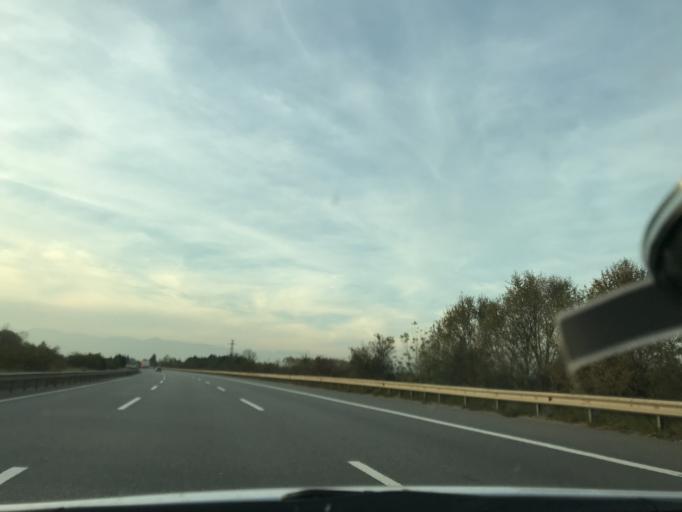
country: TR
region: Duzce
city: Cilimli
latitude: 40.8430
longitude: 31.0215
